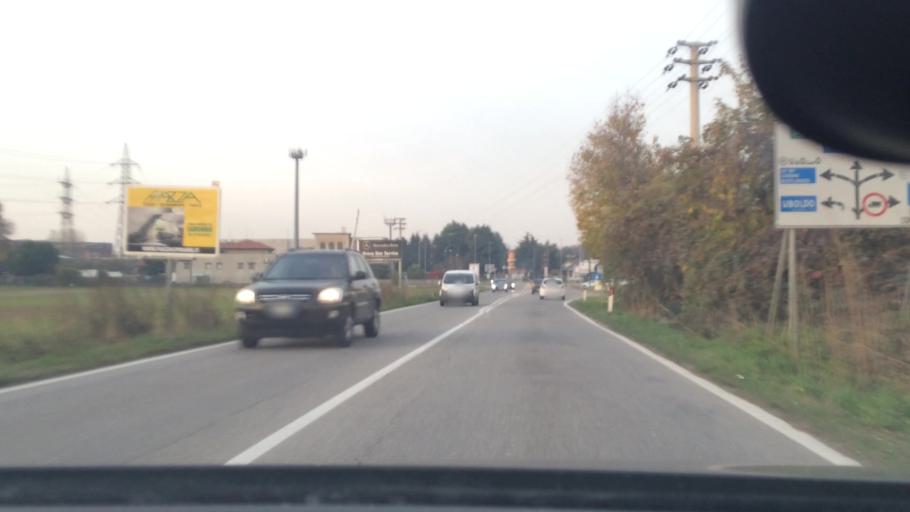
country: IT
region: Lombardy
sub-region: Provincia di Varese
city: Uboldo
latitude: 45.6181
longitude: 9.0197
